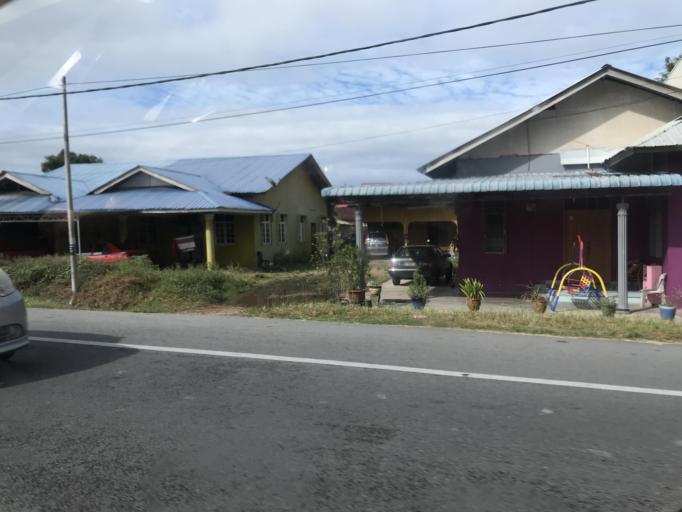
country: MY
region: Kelantan
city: Kota Bharu
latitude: 6.1225
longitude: 102.1855
